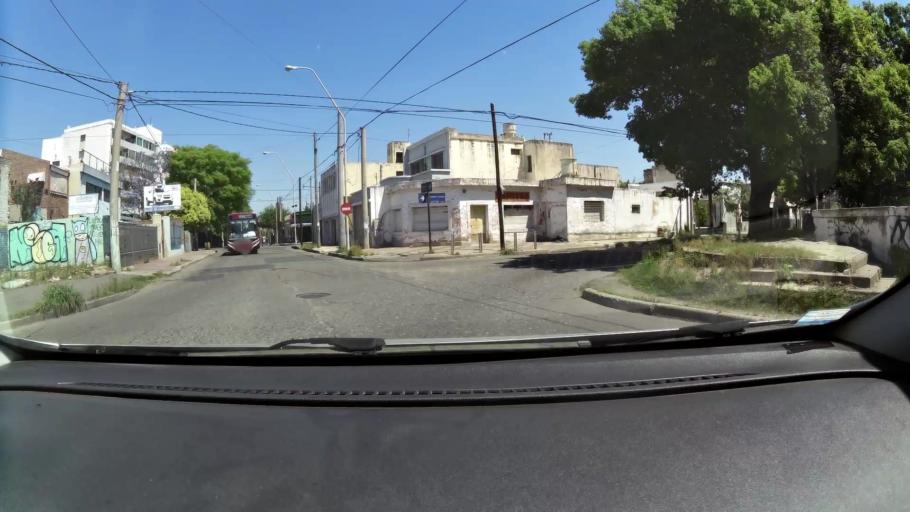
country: AR
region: Cordoba
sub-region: Departamento de Capital
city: Cordoba
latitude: -31.3915
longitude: -64.1960
